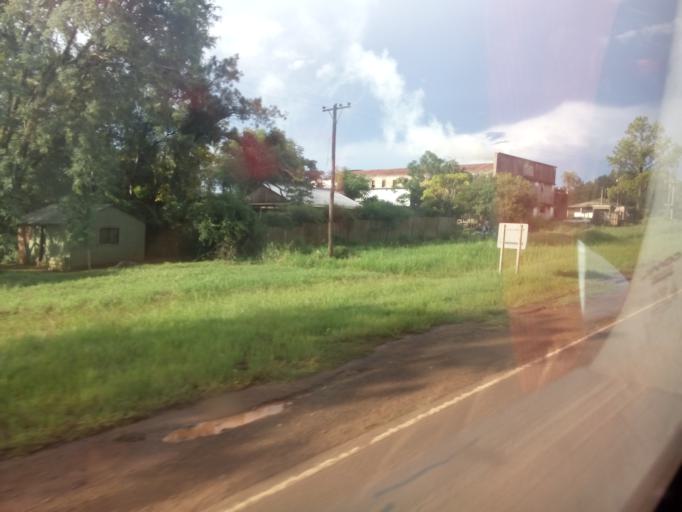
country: AR
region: Misiones
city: Santa Ana
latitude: -27.3845
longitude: -55.5882
